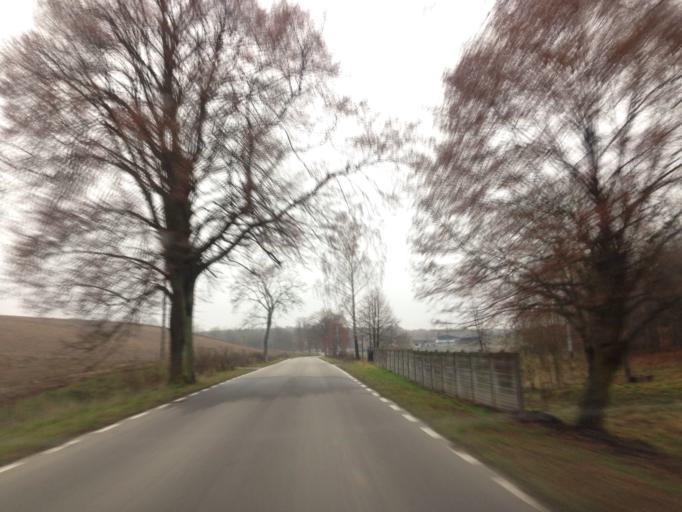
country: PL
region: Pomeranian Voivodeship
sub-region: Powiat gdanski
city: Przywidz
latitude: 54.1891
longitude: 18.3450
